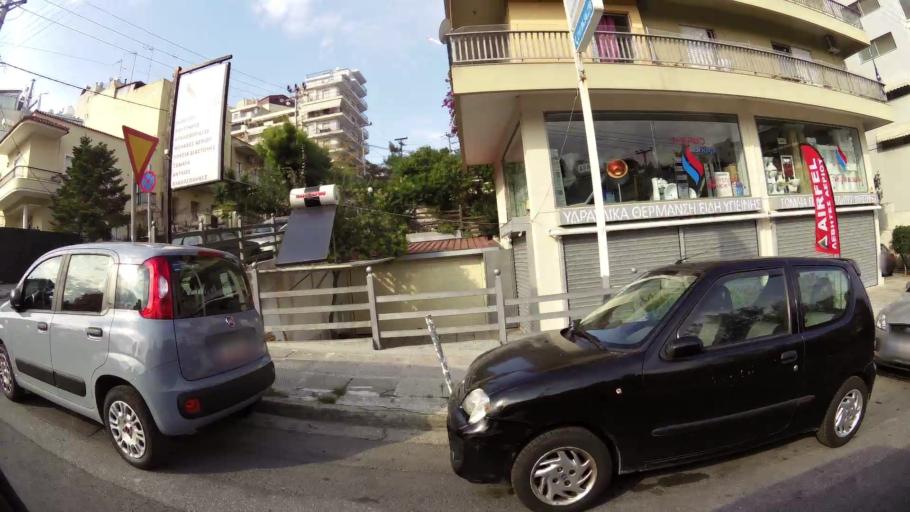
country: GR
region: Attica
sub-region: Nomarchia Athinas
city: Kipseli
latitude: 38.0081
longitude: 23.7456
